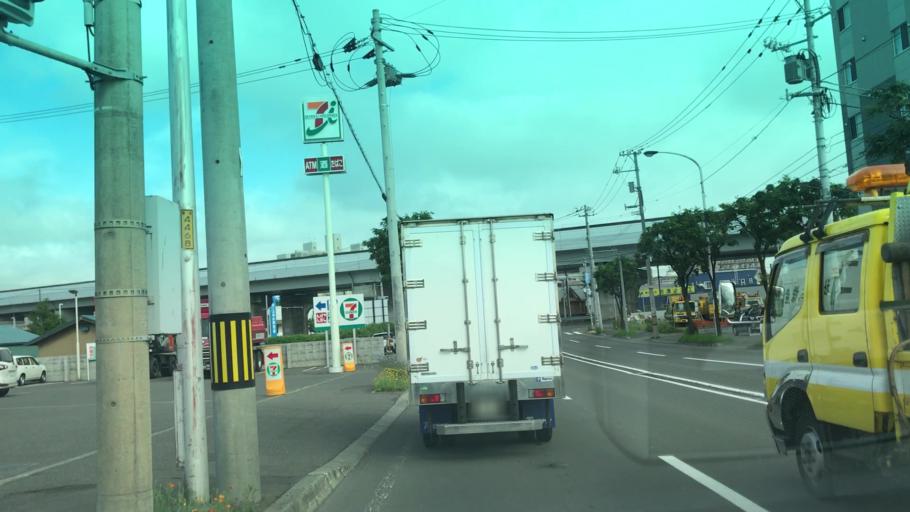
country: JP
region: Hokkaido
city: Sapporo
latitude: 43.0924
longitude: 141.2854
